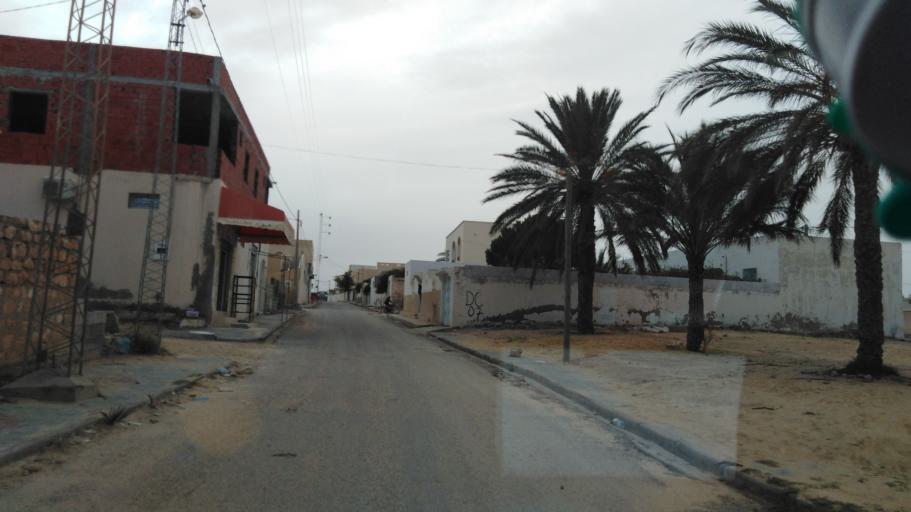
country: TN
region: Qabis
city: Gabes
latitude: 33.9560
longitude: 10.0043
